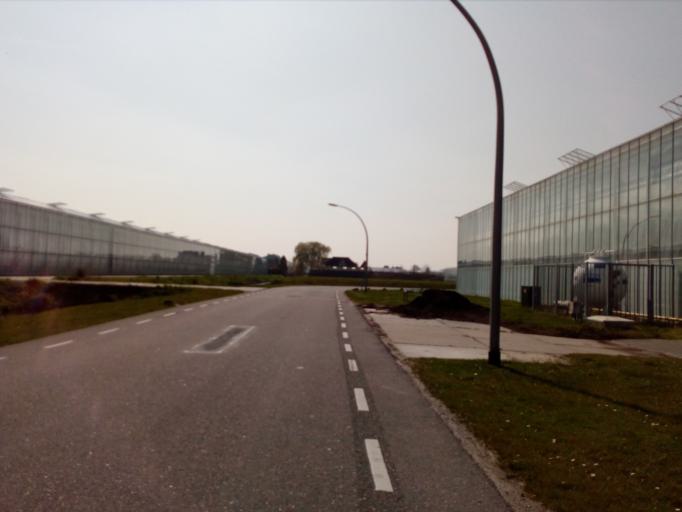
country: NL
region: South Holland
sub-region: Gemeente Lansingerland
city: Bleiswijk
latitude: 52.0301
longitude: 4.5310
